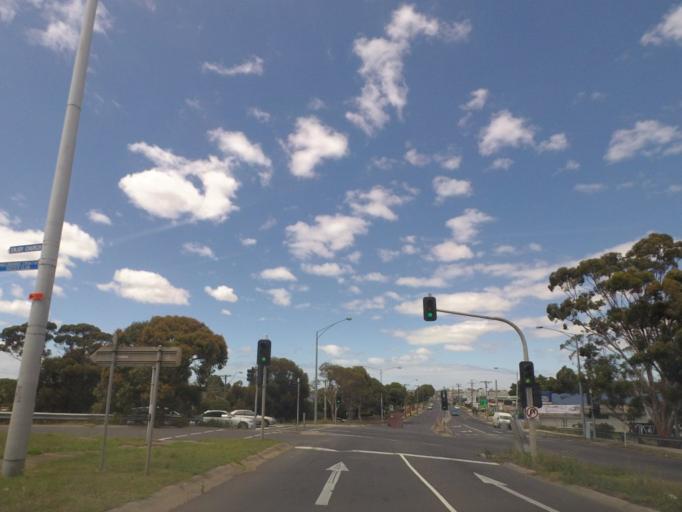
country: AU
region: Victoria
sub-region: Brimbank
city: Albion
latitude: -37.7645
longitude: 144.8311
